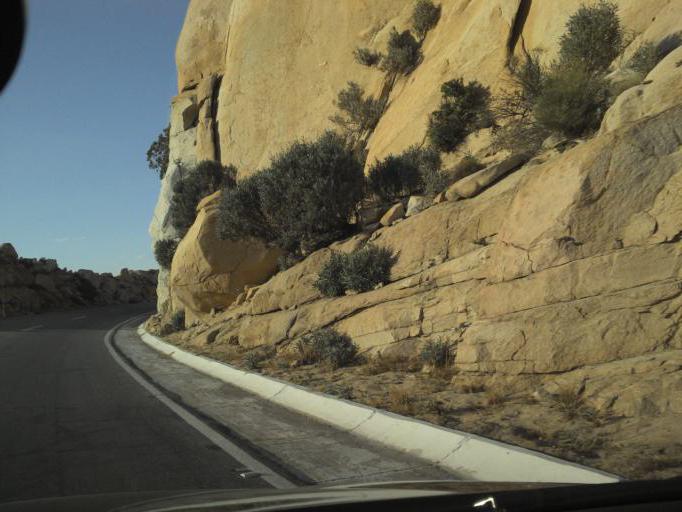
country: MX
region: Baja California
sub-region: Tecate
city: Cereso del Hongo
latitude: 32.5685
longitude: -116.0414
